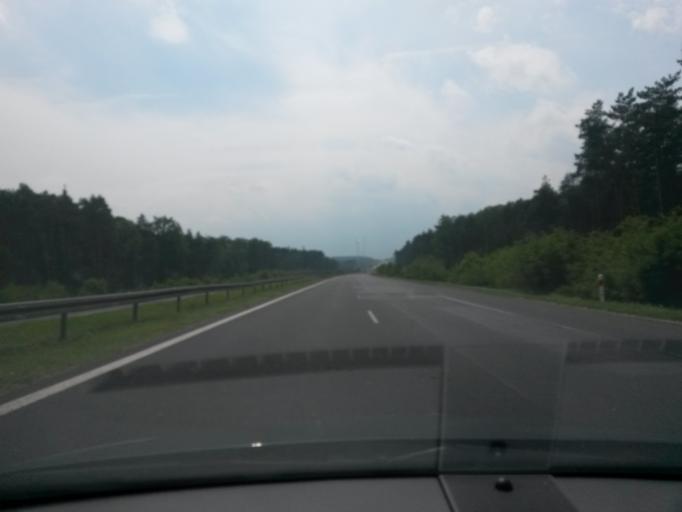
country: PL
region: Lodz Voivodeship
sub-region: Powiat radomszczanski
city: Gomunice
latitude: 51.1632
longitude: 19.4551
